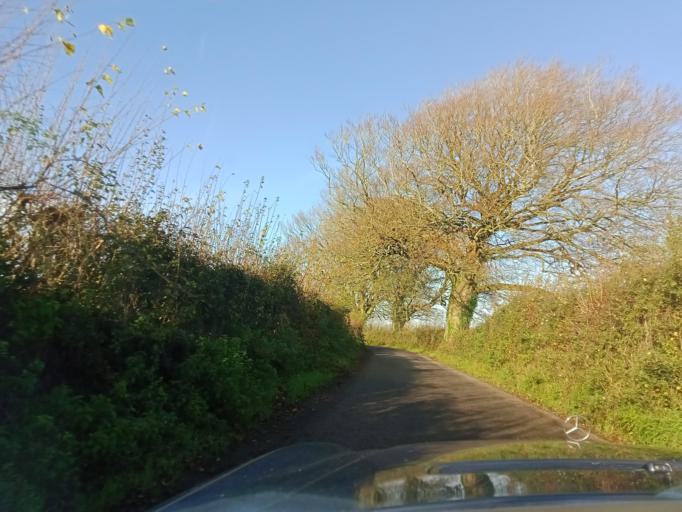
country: IE
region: Leinster
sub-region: Kilkenny
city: Mooncoin
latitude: 52.2996
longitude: -7.2094
